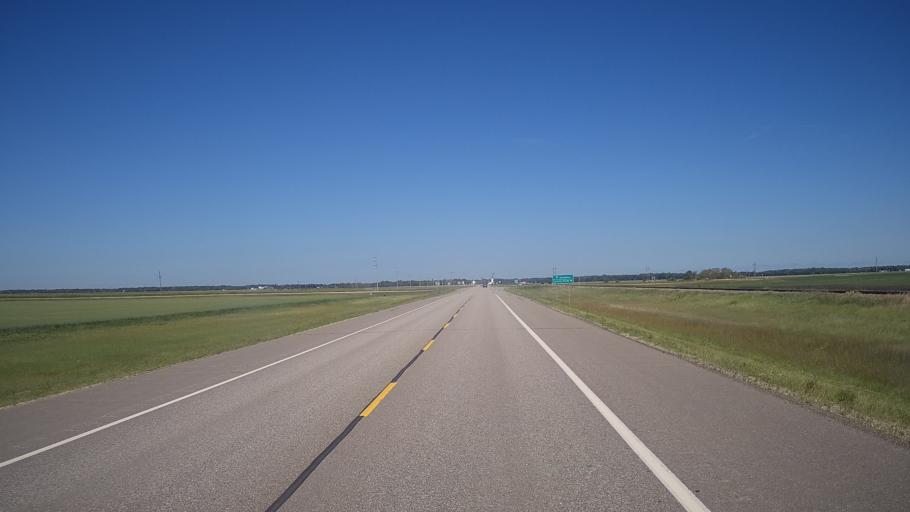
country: CA
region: Manitoba
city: Portage la Prairie
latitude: 50.1162
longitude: -98.5567
